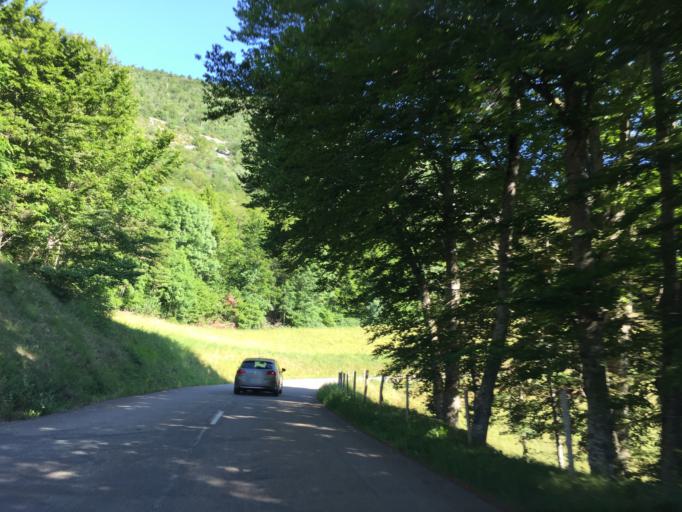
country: FR
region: Rhone-Alpes
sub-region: Departement de la Drome
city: Saint-Laurent-en-Royans
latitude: 44.9067
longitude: 5.3673
